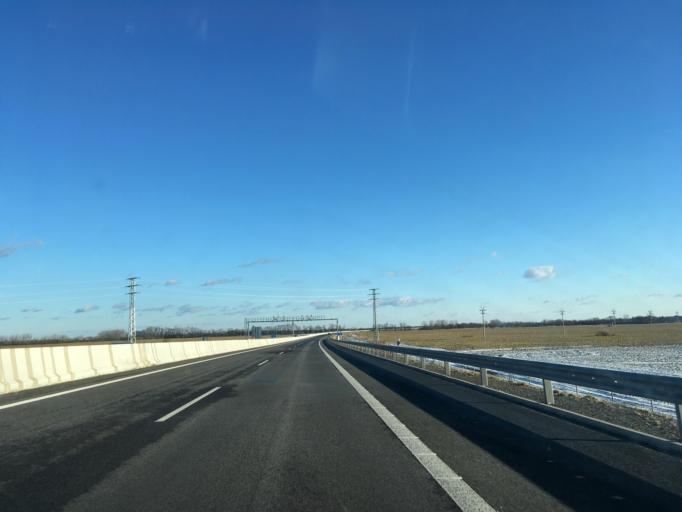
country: SK
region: Trnavsky
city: Samorin
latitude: 48.0599
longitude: 17.2972
